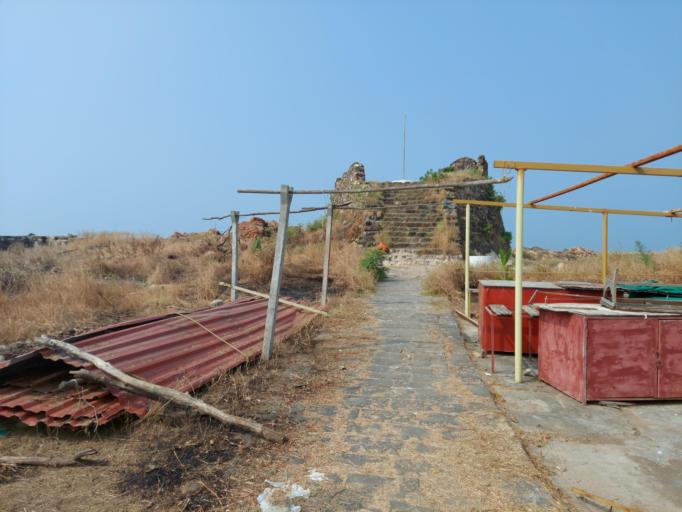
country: IN
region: Maharashtra
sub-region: Sindhudurg
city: Malvan
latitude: 16.0408
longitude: 73.4596
